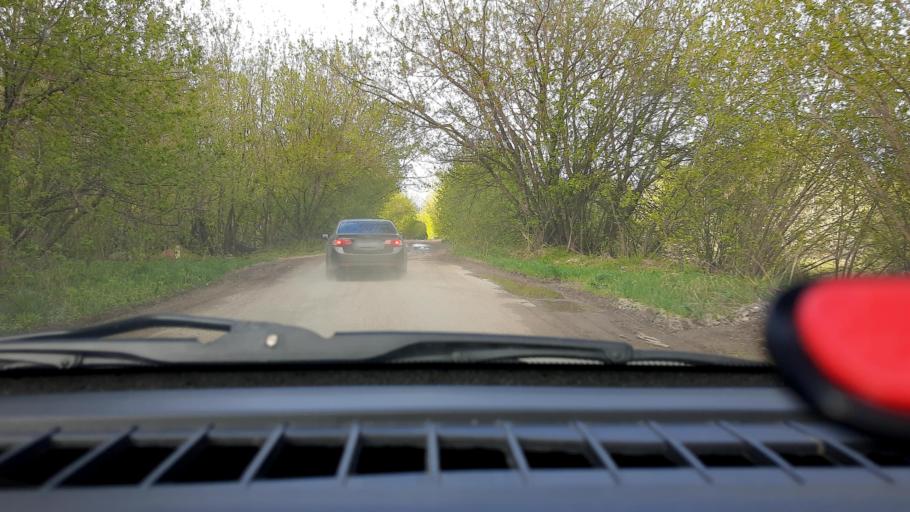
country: RU
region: Nizjnij Novgorod
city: Neklyudovo
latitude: 56.3923
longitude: 43.8450
